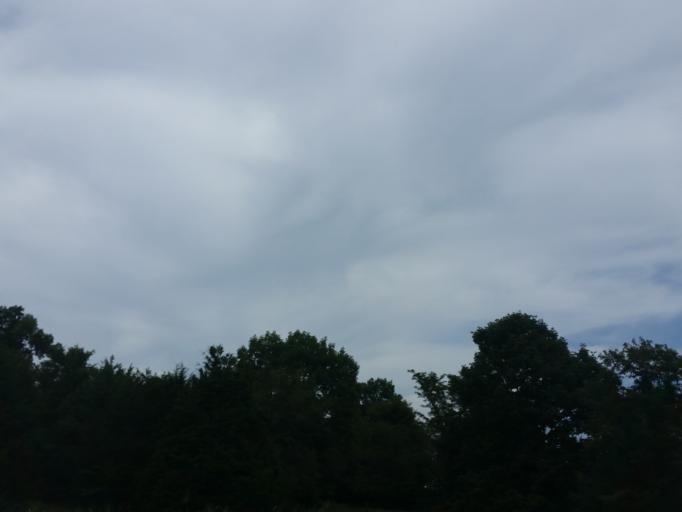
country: US
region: Kentucky
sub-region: Trigg County
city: Cadiz
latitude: 36.9526
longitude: -87.8471
